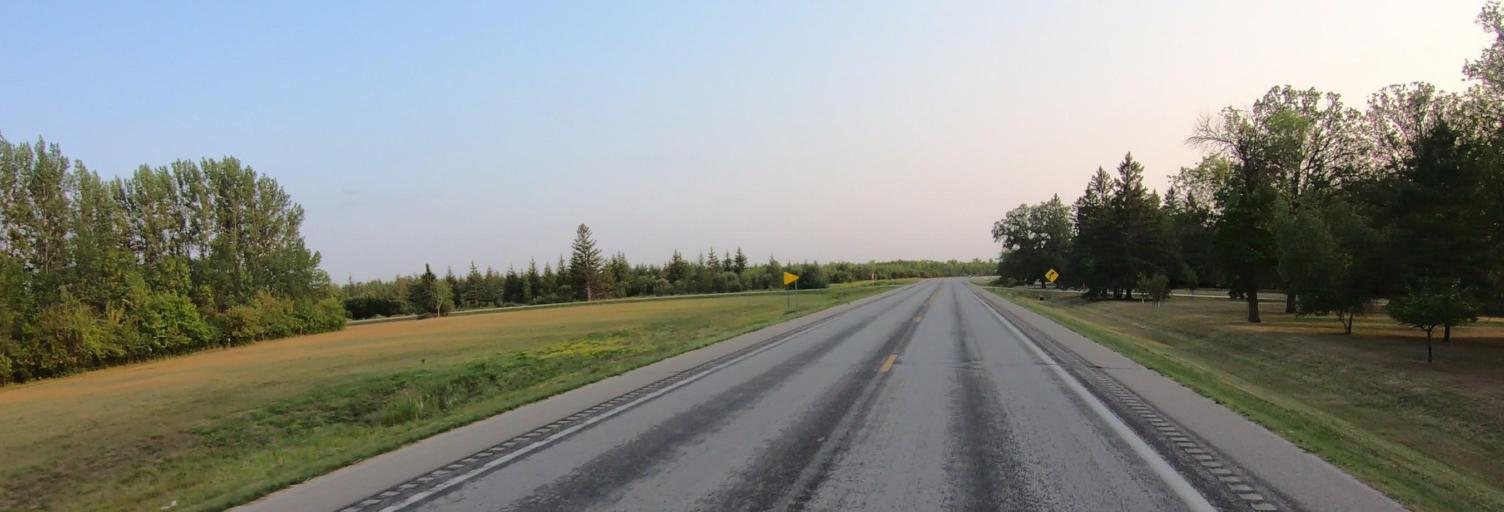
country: US
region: Minnesota
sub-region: Roseau County
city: Warroad
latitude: 48.8734
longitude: -95.3219
